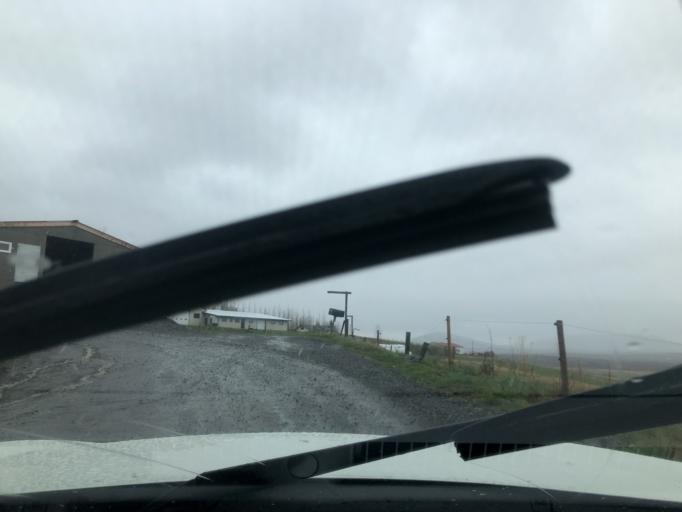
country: IS
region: South
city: Selfoss
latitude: 64.2418
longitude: -20.5482
